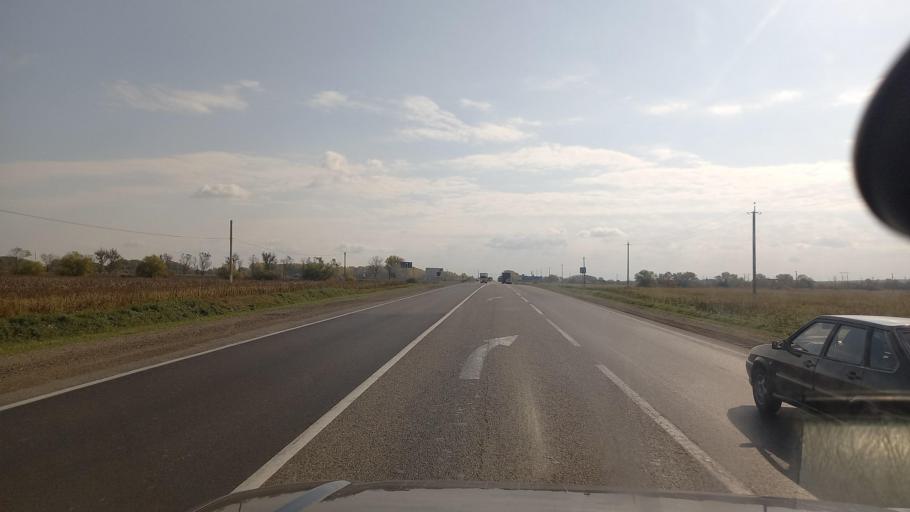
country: RU
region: Krasnodarskiy
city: Novoukrainskiy
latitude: 44.8915
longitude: 38.0694
